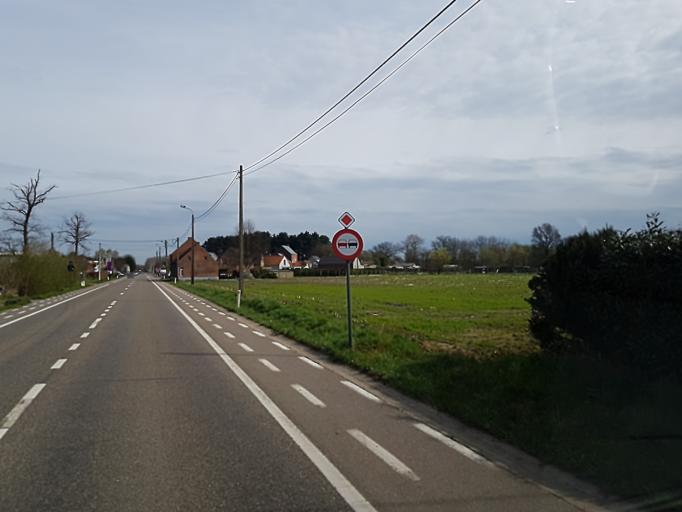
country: BE
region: Flanders
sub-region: Provincie Vlaams-Brabant
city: Aarschot
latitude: 51.0166
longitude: 4.8417
